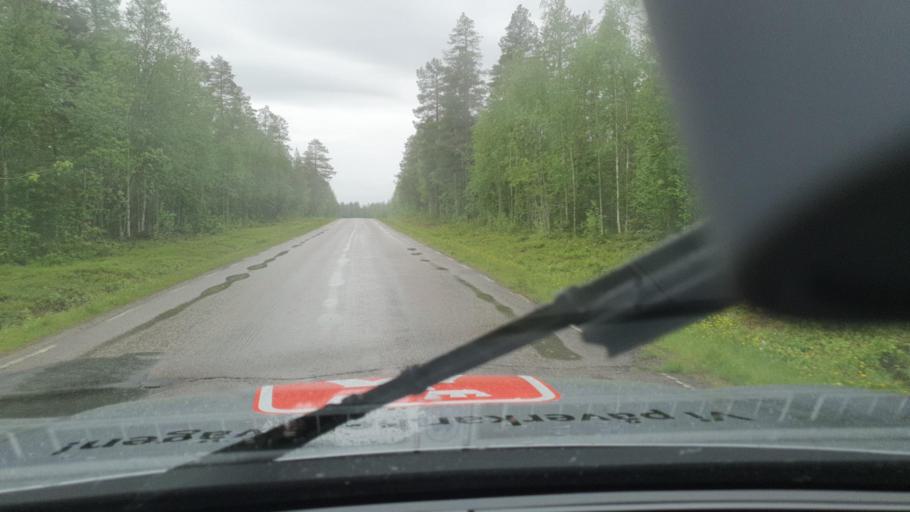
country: SE
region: Norrbotten
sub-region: Pajala Kommun
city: Pajala
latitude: 66.8256
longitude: 23.1197
